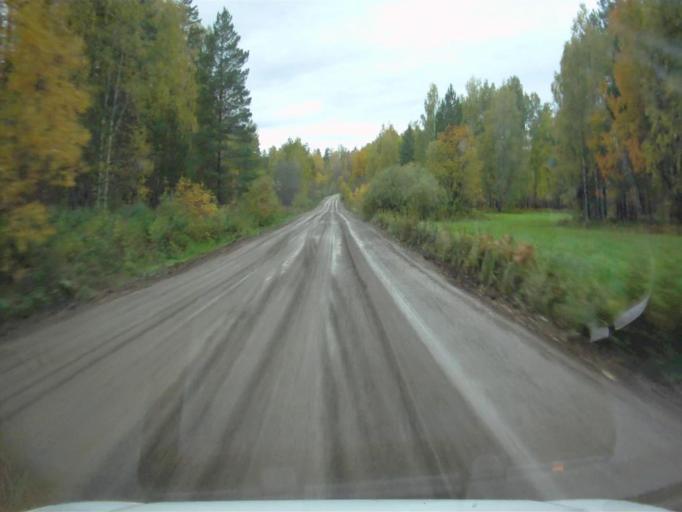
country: RU
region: Chelyabinsk
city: Nyazepetrovsk
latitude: 56.1084
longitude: 59.3781
